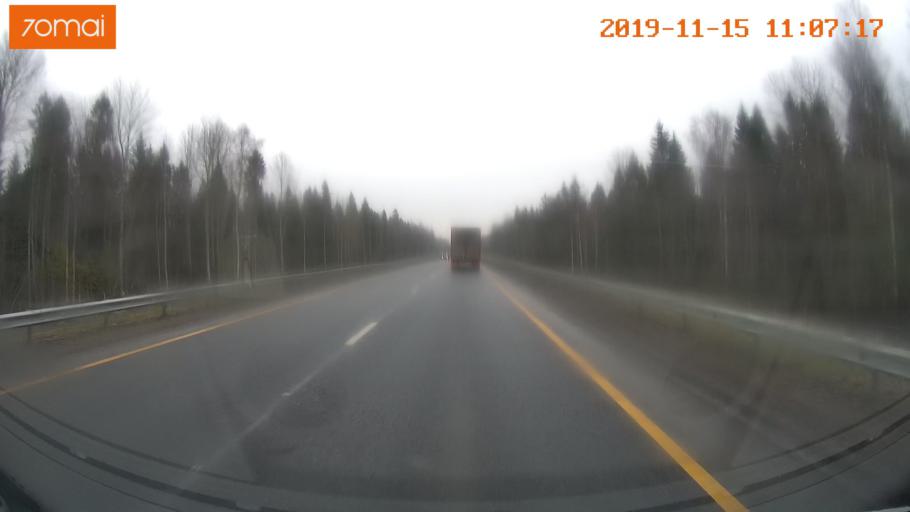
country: RU
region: Vologda
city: Chebsara
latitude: 59.1194
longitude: 39.0463
